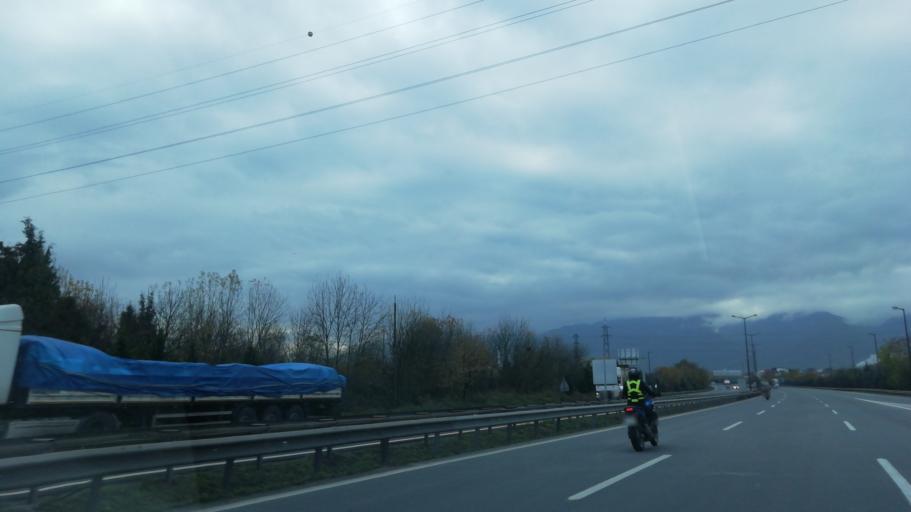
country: TR
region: Kocaeli
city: Kosekoy
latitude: 40.7464
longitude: 30.0416
